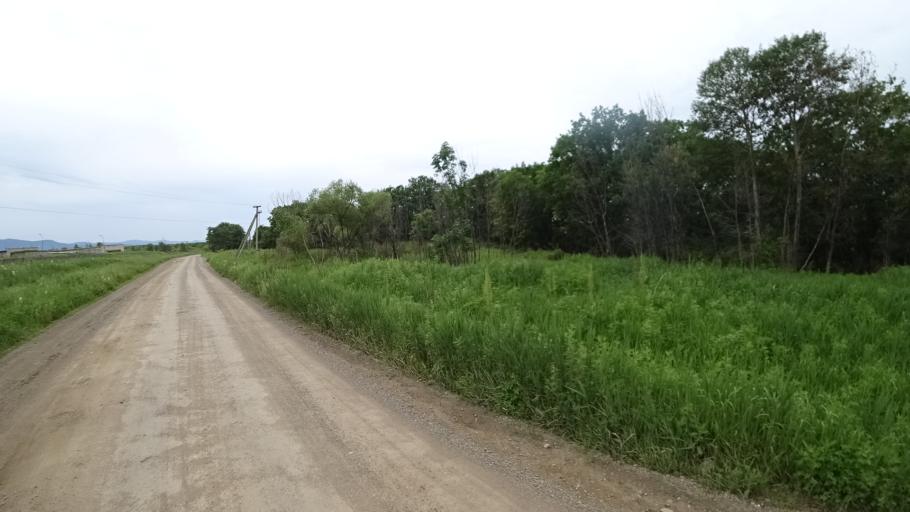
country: RU
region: Primorskiy
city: Arsen'yev
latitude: 44.2012
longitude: 133.3110
